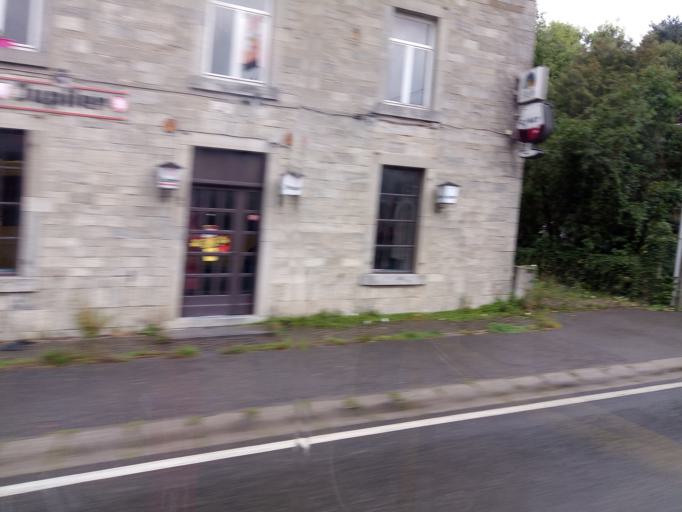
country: BE
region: Wallonia
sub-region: Province du Luxembourg
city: Hotton
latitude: 50.2583
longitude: 5.4715
